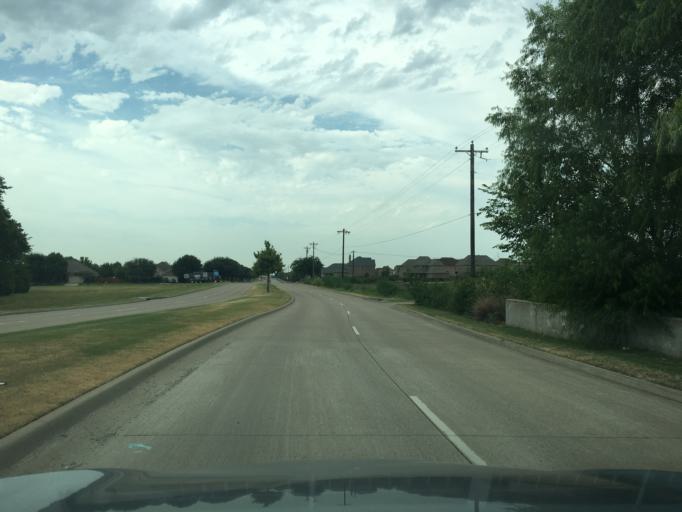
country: US
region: Texas
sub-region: Collin County
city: Parker
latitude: 33.0424
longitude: -96.5946
